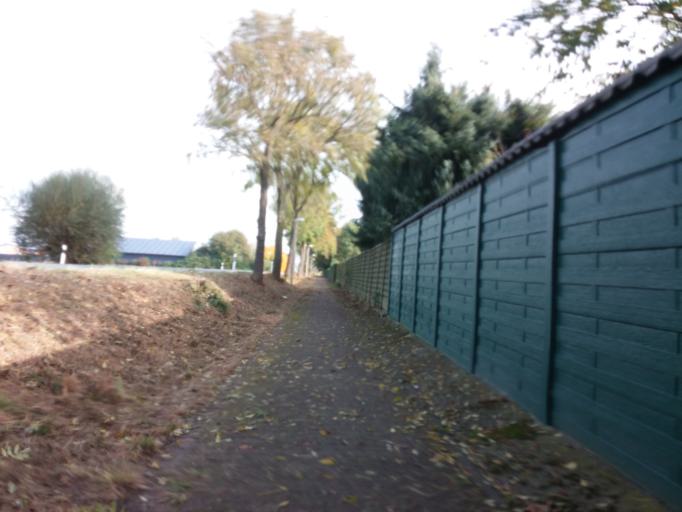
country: DE
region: North Rhine-Westphalia
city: Dorsten
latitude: 51.6343
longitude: 7.0055
